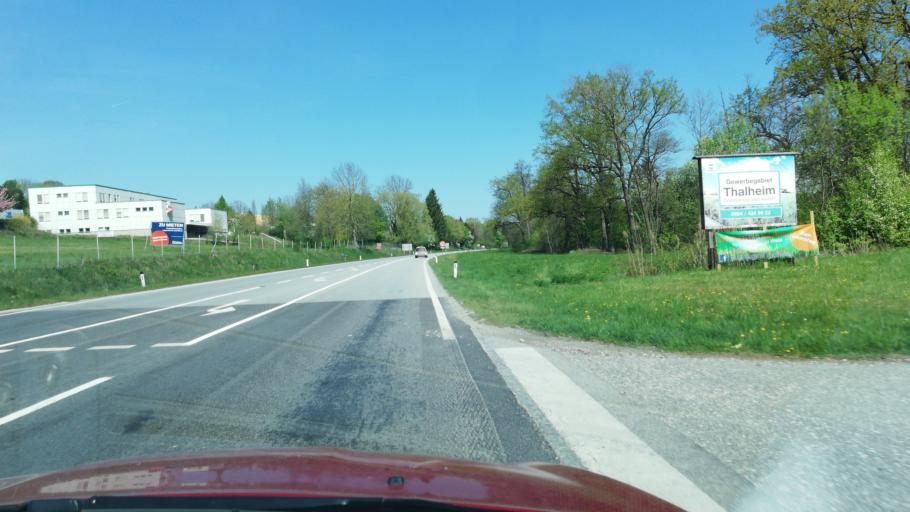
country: AT
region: Upper Austria
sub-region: Wels-Land
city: Thalheim bei Wels
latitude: 48.1382
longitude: 14.0470
